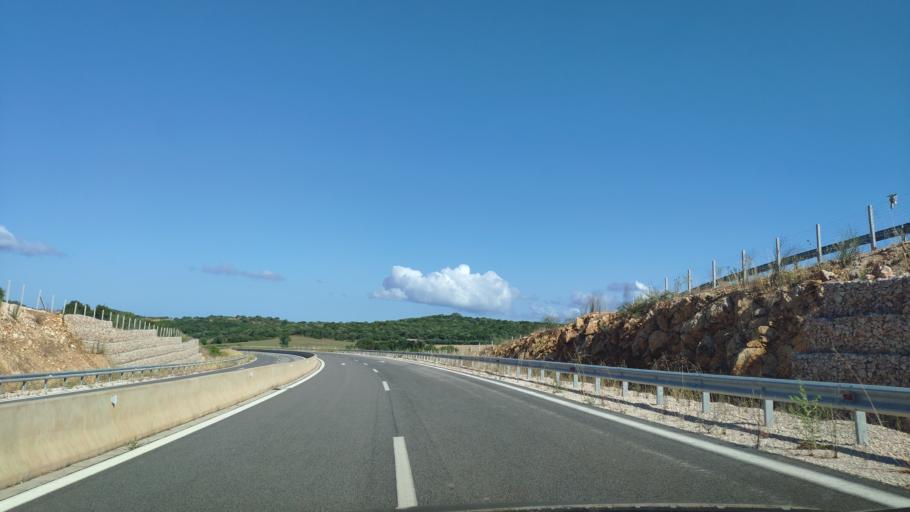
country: GR
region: West Greece
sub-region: Nomos Aitolias kai Akarnanias
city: Vonitsa
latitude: 38.9099
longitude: 20.8468
